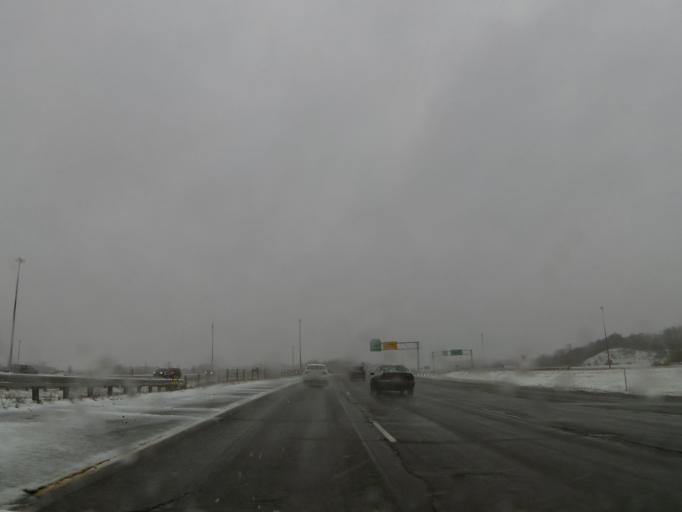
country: US
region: Minnesota
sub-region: Dakota County
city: Mendota Heights
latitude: 44.8624
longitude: -93.1480
